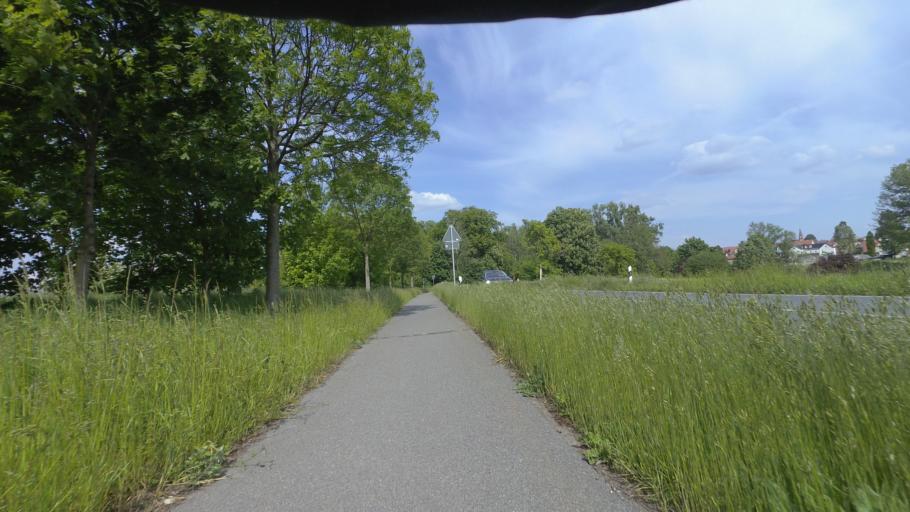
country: DE
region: Saxony-Anhalt
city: Hotensleben
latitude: 52.1232
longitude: 11.0093
